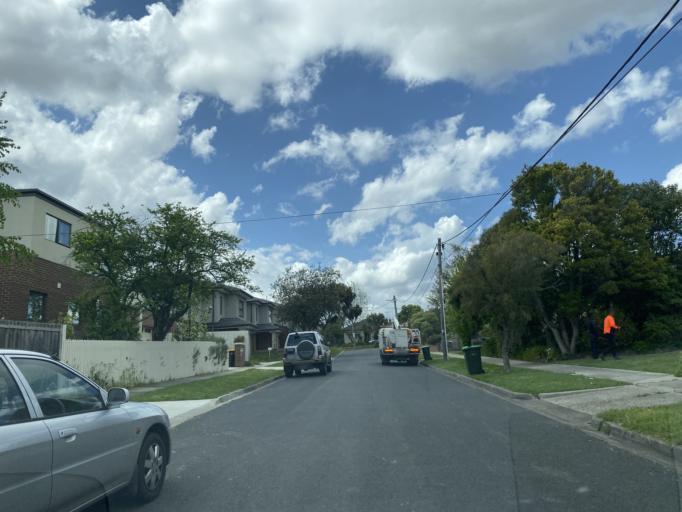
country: AU
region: Victoria
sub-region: Whitehorse
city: Burwood
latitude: -37.8543
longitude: 145.1117
